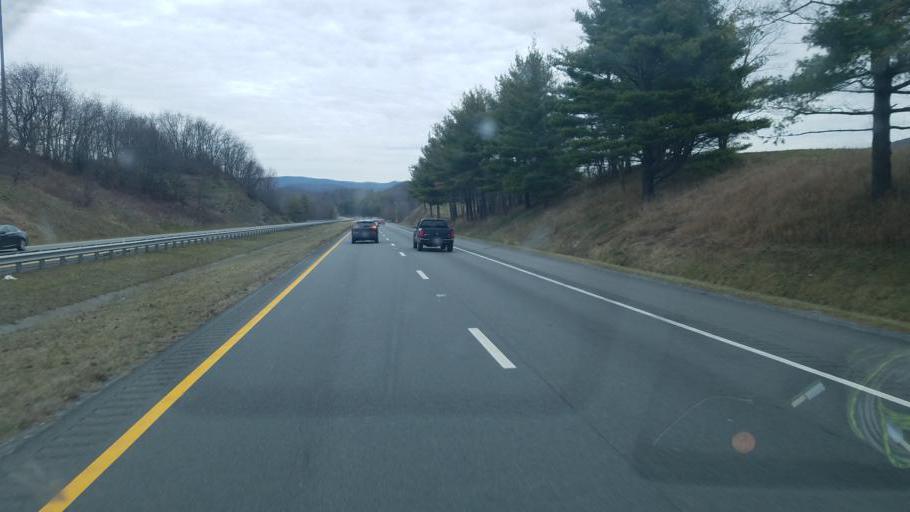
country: US
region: Virginia
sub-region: Bland County
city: Bland
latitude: 37.0542
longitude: -81.1344
